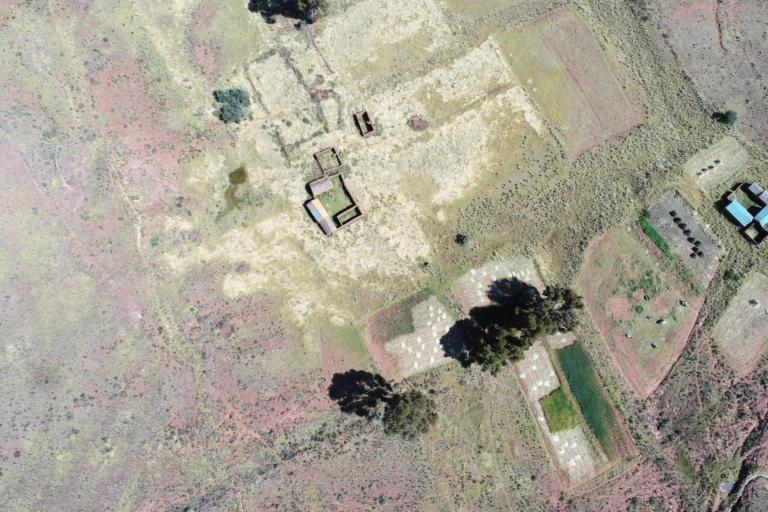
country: BO
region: La Paz
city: Tiahuanaco
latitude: -16.6073
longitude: -68.7720
